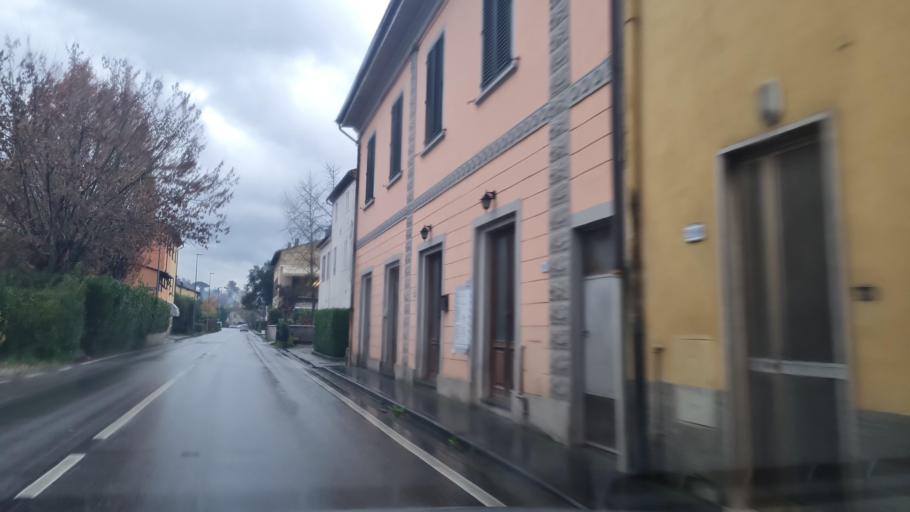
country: IT
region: Tuscany
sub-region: Provincia di Lucca
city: Lucca
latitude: 43.8615
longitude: 10.4828
